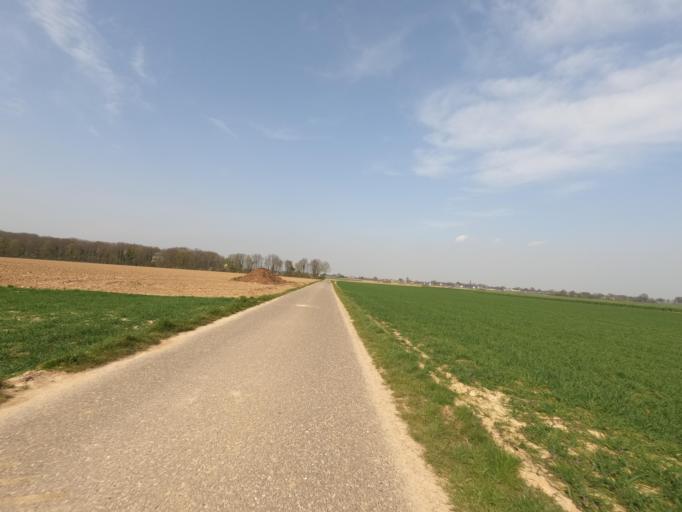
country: DE
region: North Rhine-Westphalia
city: Erkelenz
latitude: 51.0478
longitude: 6.3412
